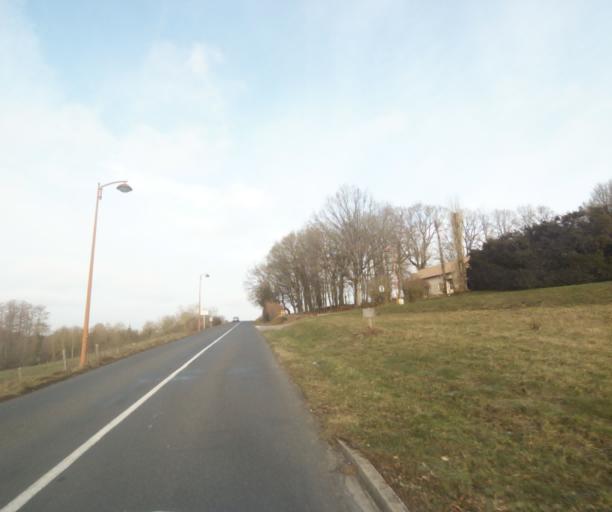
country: FR
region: Champagne-Ardenne
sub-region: Departement de la Marne
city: Sermaize-les-Bains
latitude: 48.7238
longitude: 4.9402
